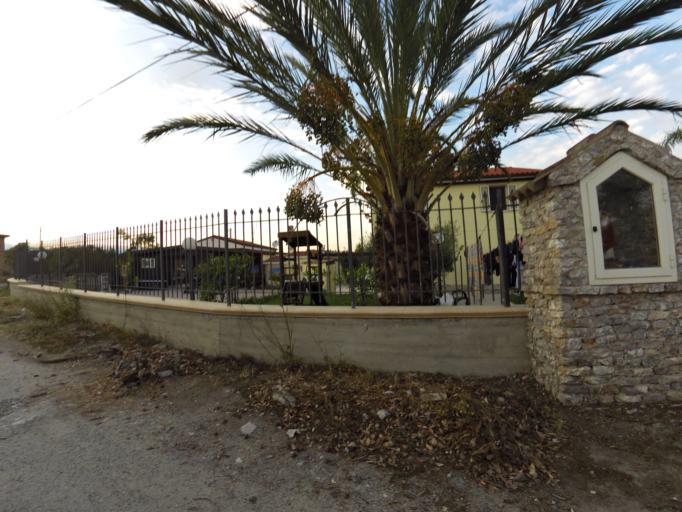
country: IT
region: Calabria
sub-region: Provincia di Reggio Calabria
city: Monasterace Marina
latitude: 38.4512
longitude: 16.5778
